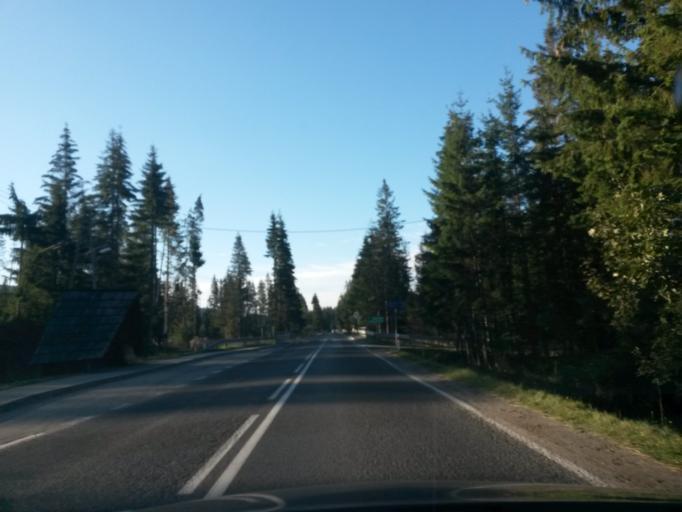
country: PL
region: Lesser Poland Voivodeship
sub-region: Powiat tatrzanski
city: Koscielisko
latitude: 49.2894
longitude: 19.8508
